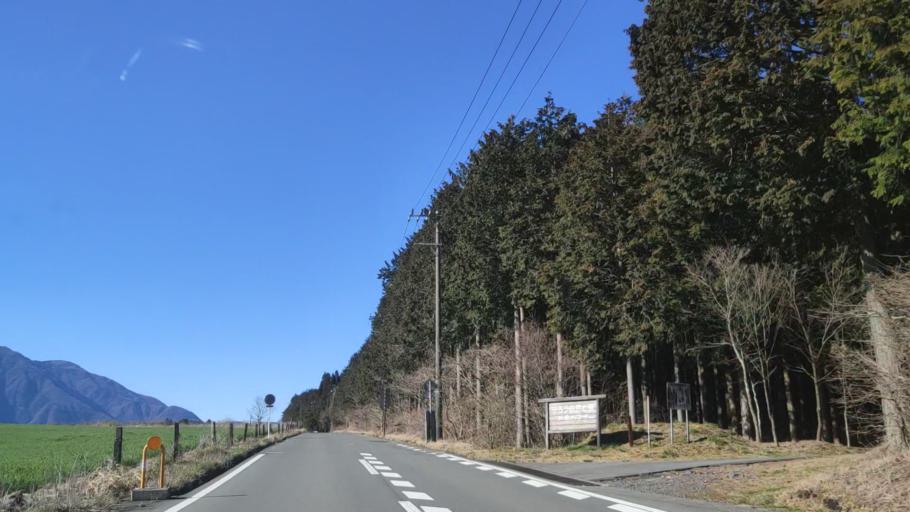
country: JP
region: Yamanashi
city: Fujikawaguchiko
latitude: 35.3784
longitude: 138.6051
